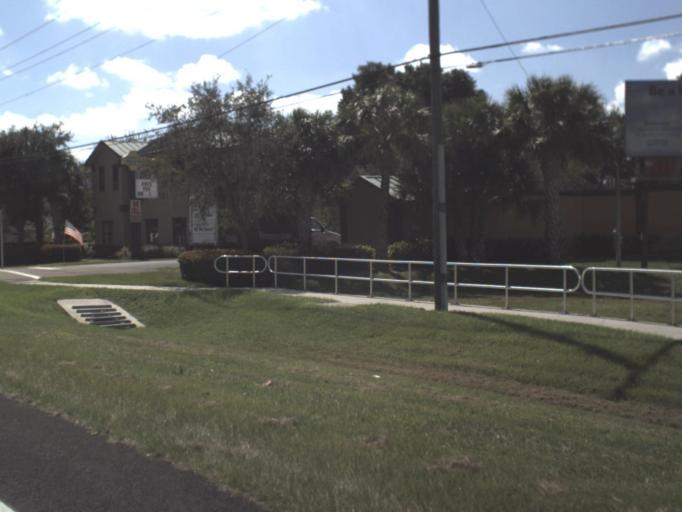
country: US
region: Florida
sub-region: Lee County
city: Estero
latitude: 26.4564
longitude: -81.8248
